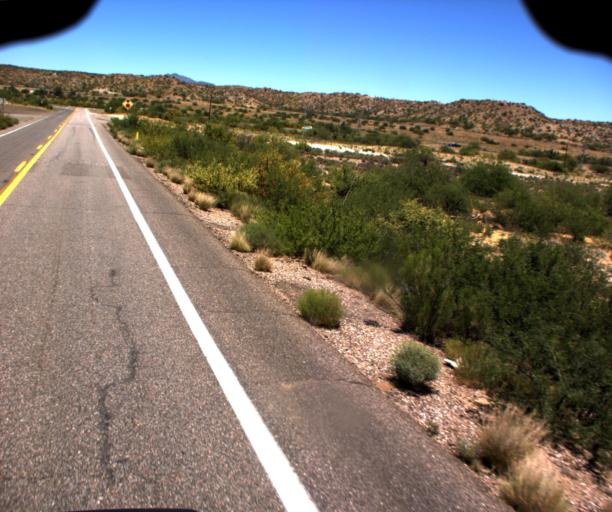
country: US
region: Arizona
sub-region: Gila County
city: Globe
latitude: 33.3705
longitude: -110.7378
